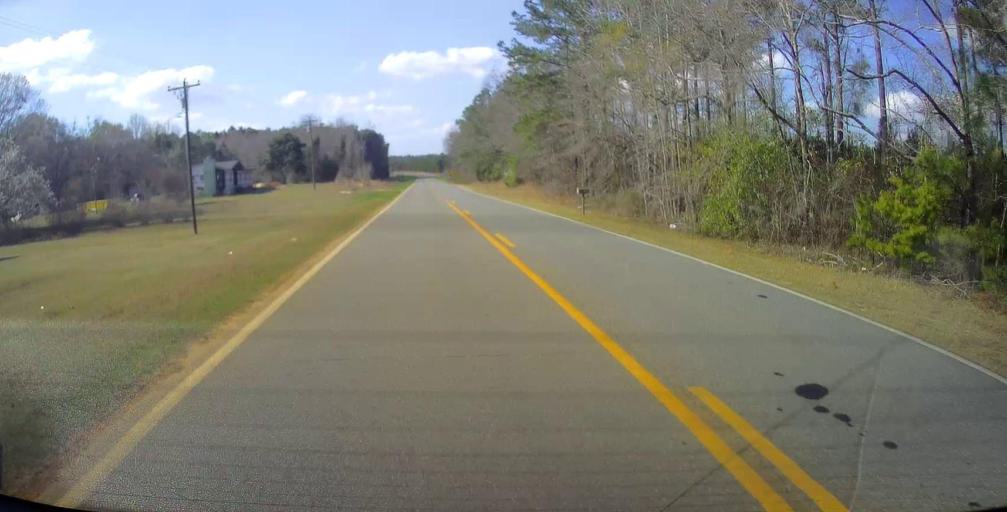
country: US
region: Georgia
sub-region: Laurens County
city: Dublin
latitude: 32.5814
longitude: -83.0530
